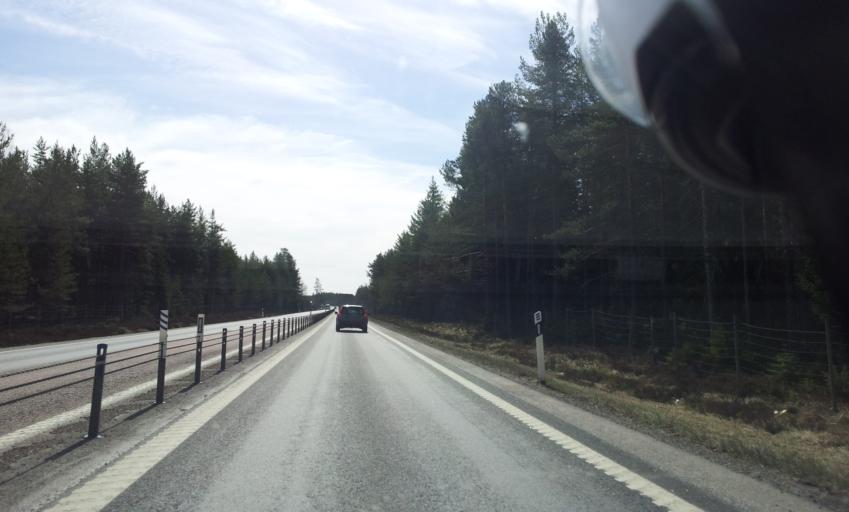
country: SE
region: Gaevleborg
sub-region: Gavle Kommun
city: Norrsundet
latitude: 61.0490
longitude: 16.9589
